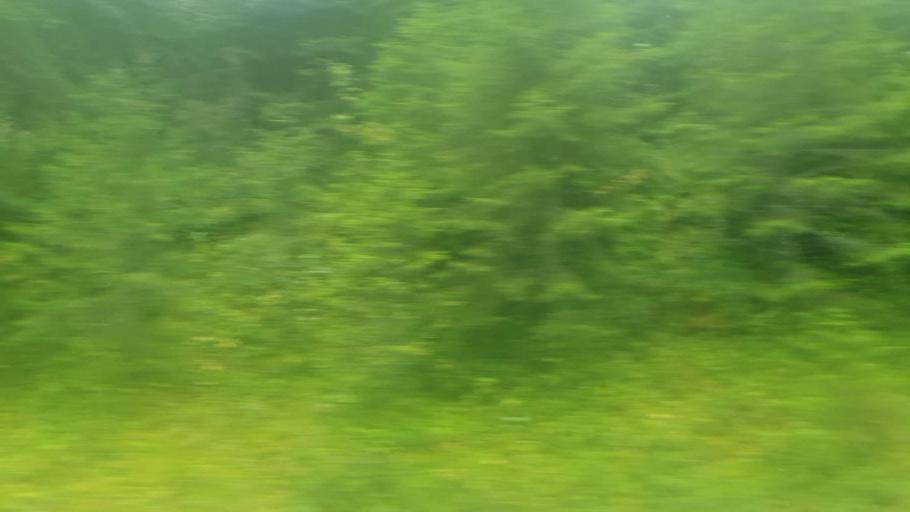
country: NO
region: Nord-Trondelag
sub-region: Levanger
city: Skogn
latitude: 63.6187
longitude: 11.2182
